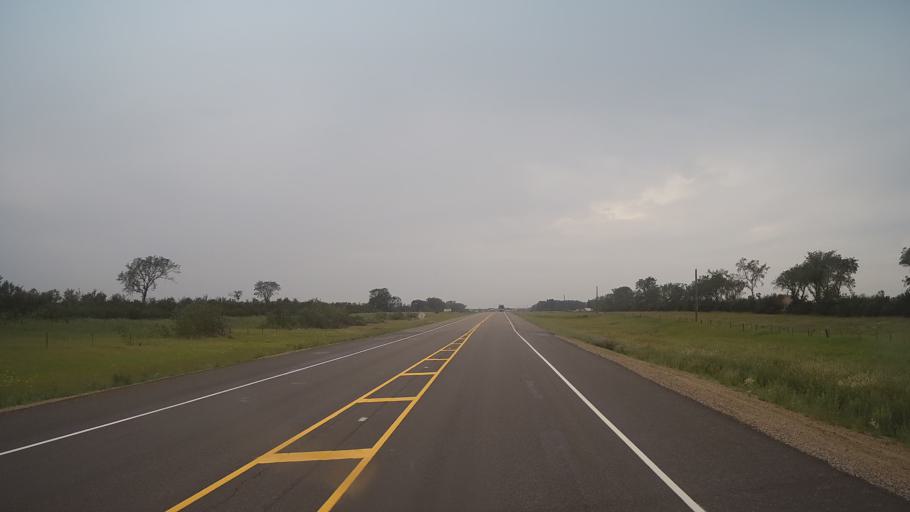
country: CA
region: Saskatchewan
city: Dalmeny
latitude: 52.1293
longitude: -106.8651
